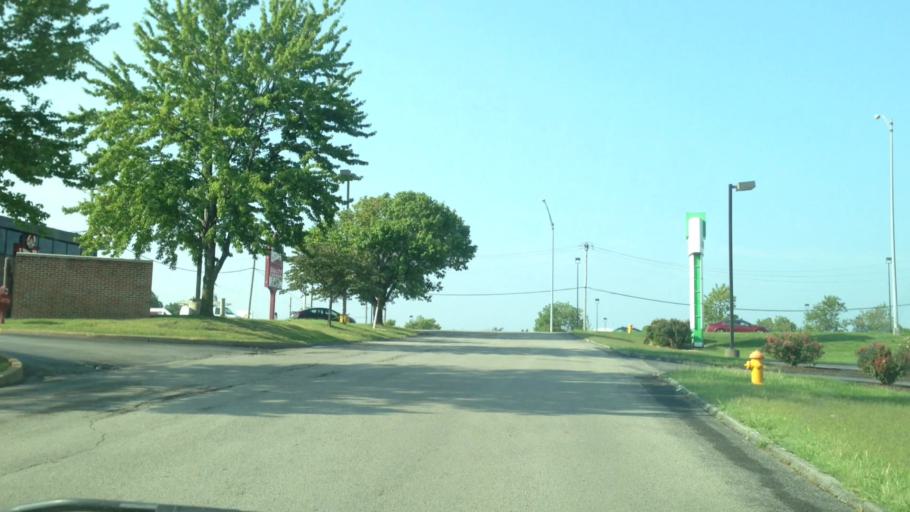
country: US
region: Missouri
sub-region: Saint Louis County
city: Mehlville
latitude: 38.5113
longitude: -90.3340
